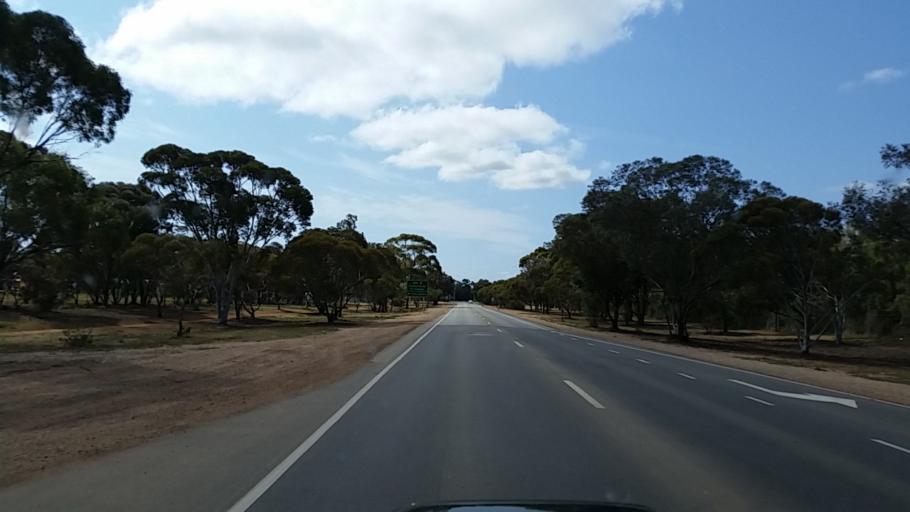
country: AU
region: South Australia
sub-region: Port Pirie City and Dists
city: Port Pirie
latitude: -33.2088
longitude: 138.0116
